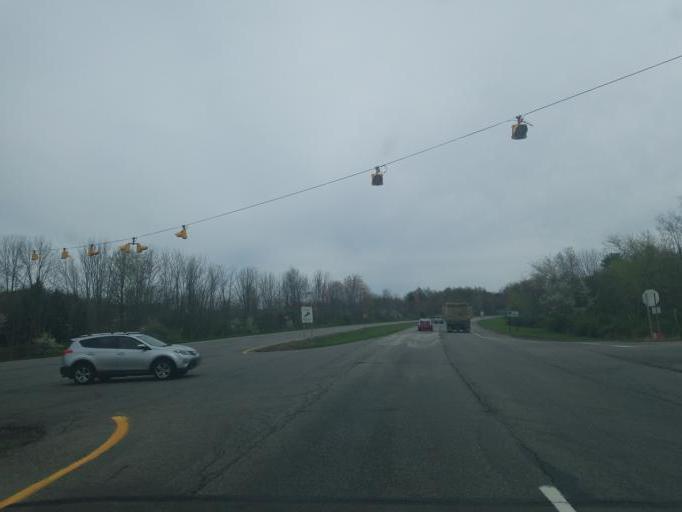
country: US
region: Ohio
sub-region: Wayne County
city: Doylestown
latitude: 40.9885
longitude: -81.6789
